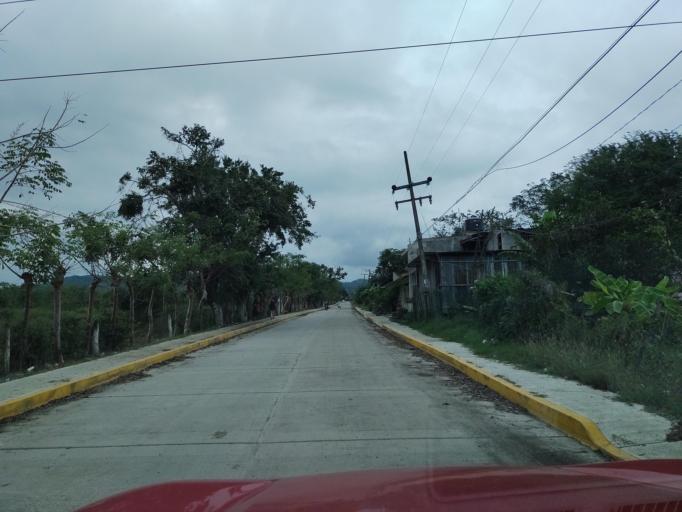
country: MX
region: Veracruz
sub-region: Papantla
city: El Chote
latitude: 20.4314
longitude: -97.3810
